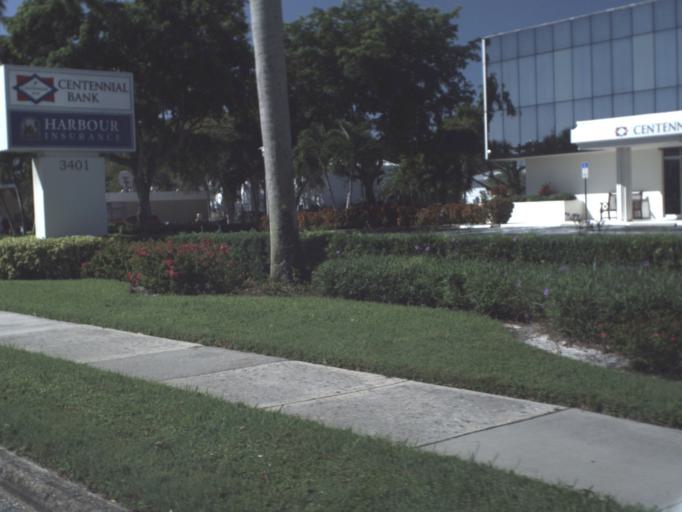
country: US
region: Florida
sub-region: Collier County
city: Pine Ridge
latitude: 26.1890
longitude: -81.8001
